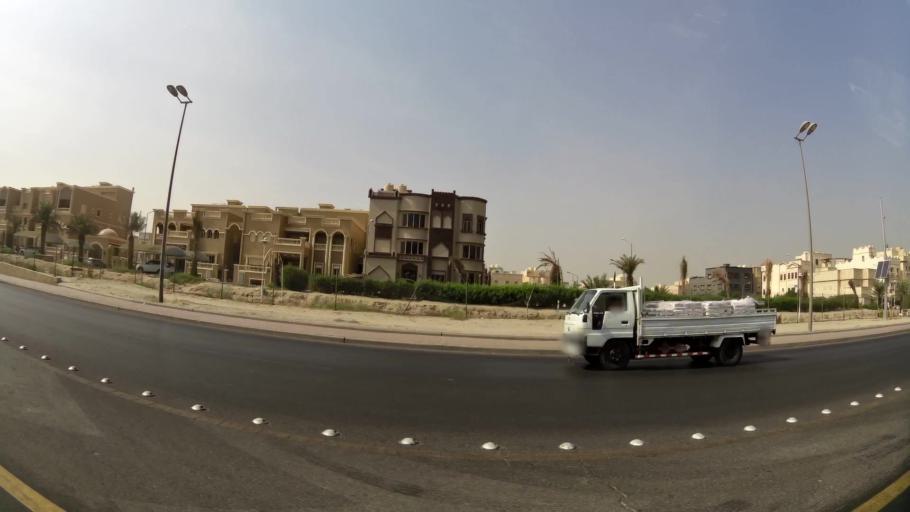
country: KW
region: Al Farwaniyah
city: Al Farwaniyah
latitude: 29.2705
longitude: 47.9512
